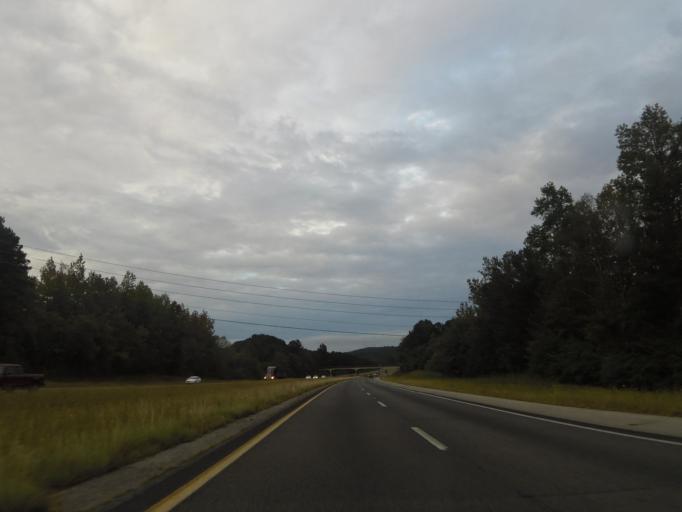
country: US
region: Alabama
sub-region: Jefferson County
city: Argo
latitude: 33.7204
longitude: -86.5122
